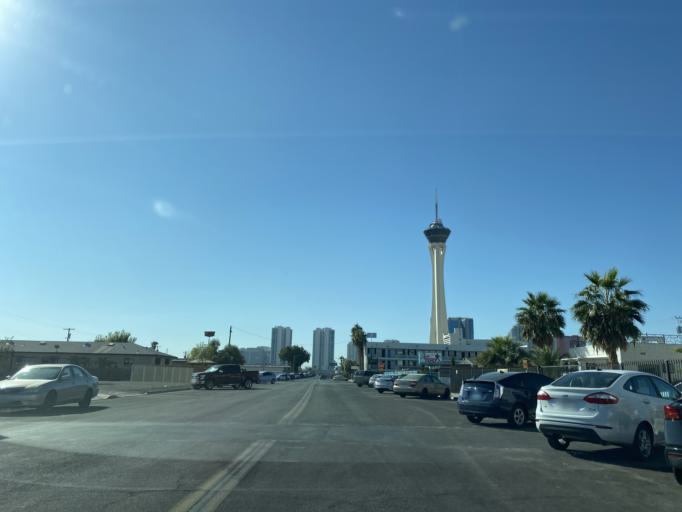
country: US
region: Nevada
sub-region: Clark County
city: Las Vegas
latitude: 36.1557
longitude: -115.1525
